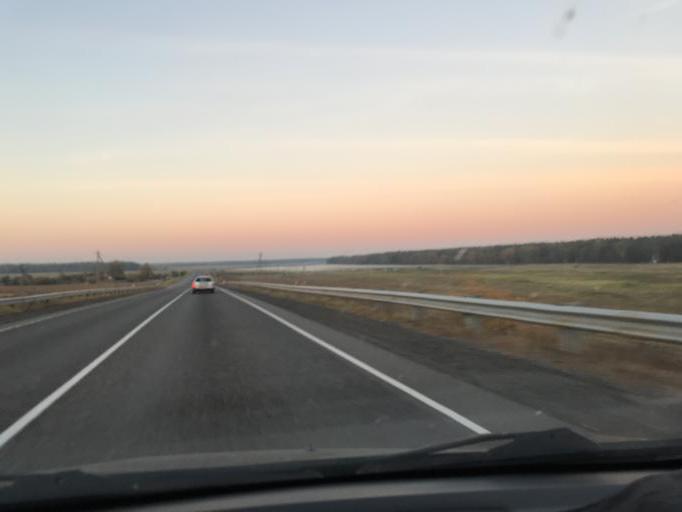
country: BY
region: Mogilev
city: Babruysk
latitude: 53.1833
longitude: 29.0483
